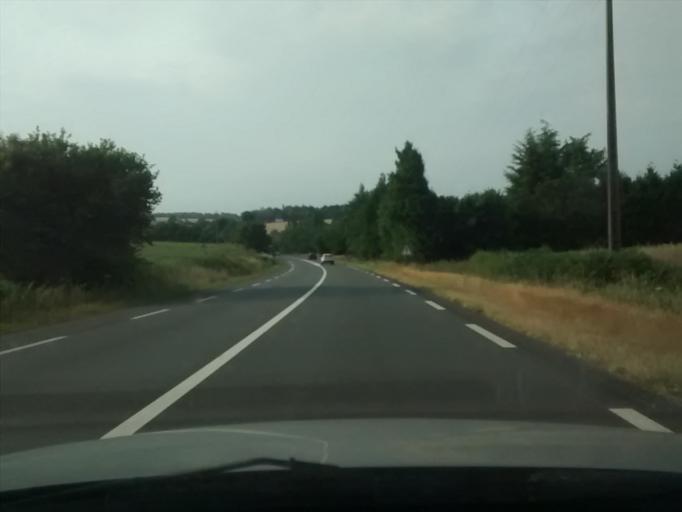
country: FR
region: Brittany
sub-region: Departement d'Ille-et-Vilaine
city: Etrelles
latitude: 48.0785
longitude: -1.2004
